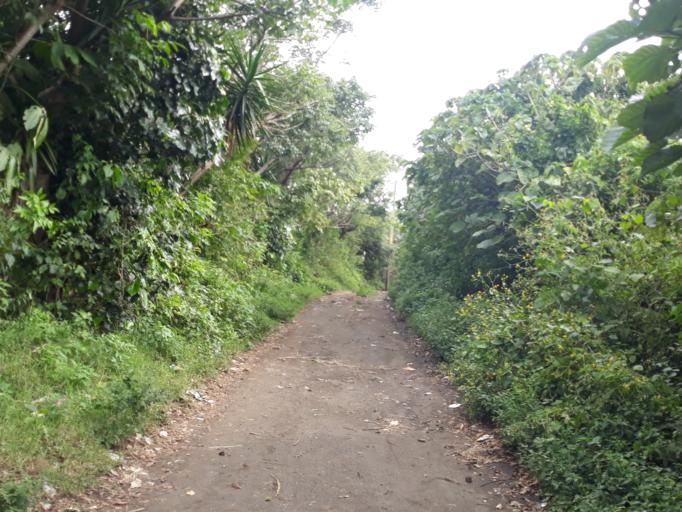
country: GT
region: Escuintla
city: San Vicente Pacaya
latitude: 14.3659
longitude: -90.5533
